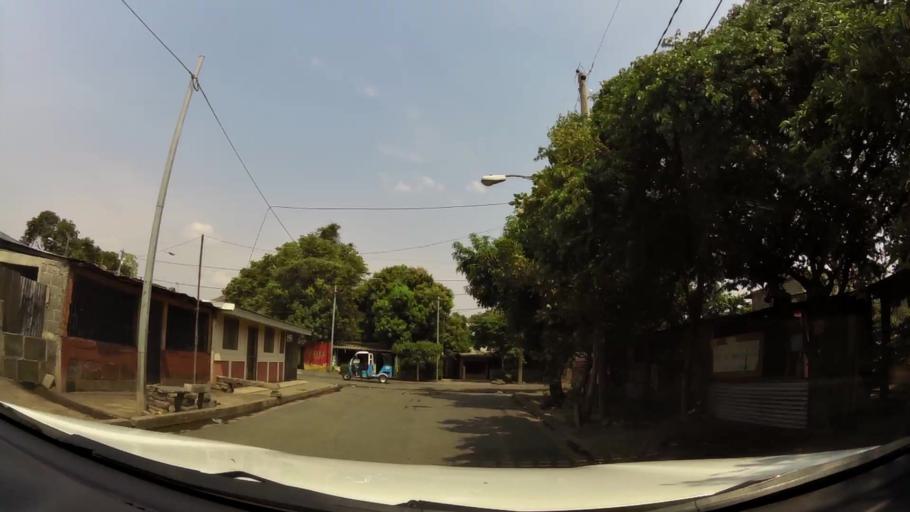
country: NI
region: Managua
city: Ciudad Sandino
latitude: 12.1270
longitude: -86.3141
